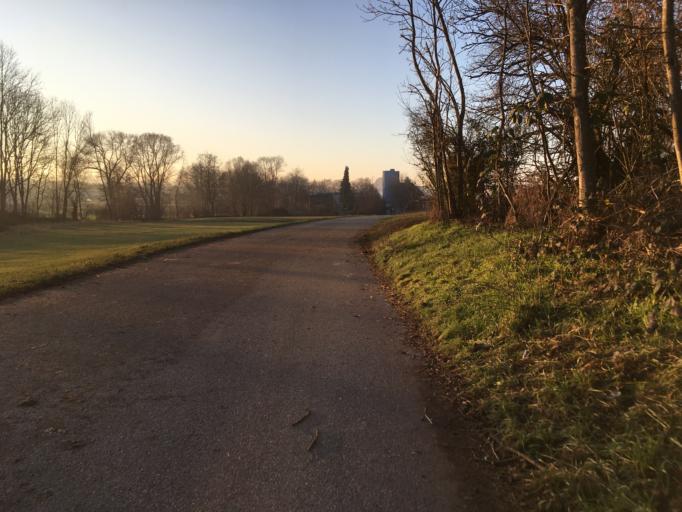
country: DE
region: Baden-Wuerttemberg
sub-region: Regierungsbezirk Stuttgart
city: Ellhofen
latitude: 49.1535
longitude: 9.3148
